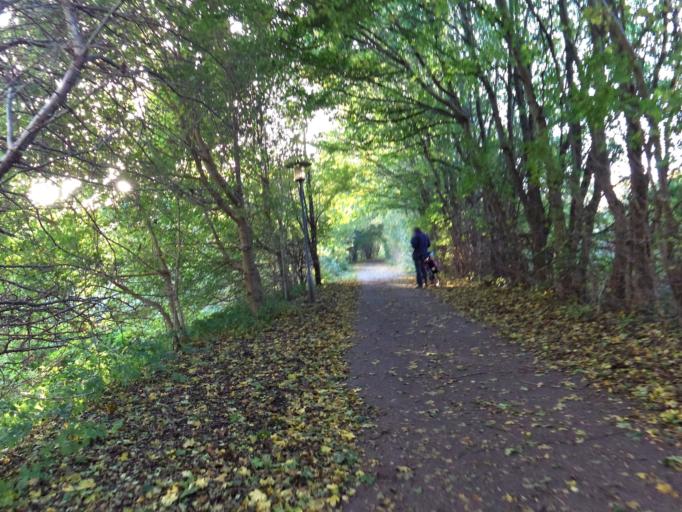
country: DK
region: Central Jutland
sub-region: Arhus Kommune
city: Stavtrup
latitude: 56.1277
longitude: 10.1351
